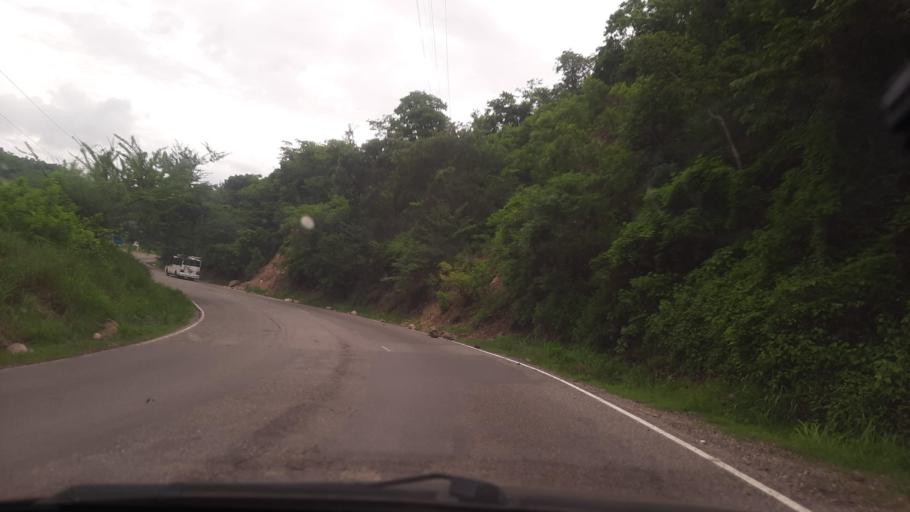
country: GT
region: Chiquimula
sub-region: Municipio de Chiquimula
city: Chiquimula
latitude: 14.8720
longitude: -89.5129
